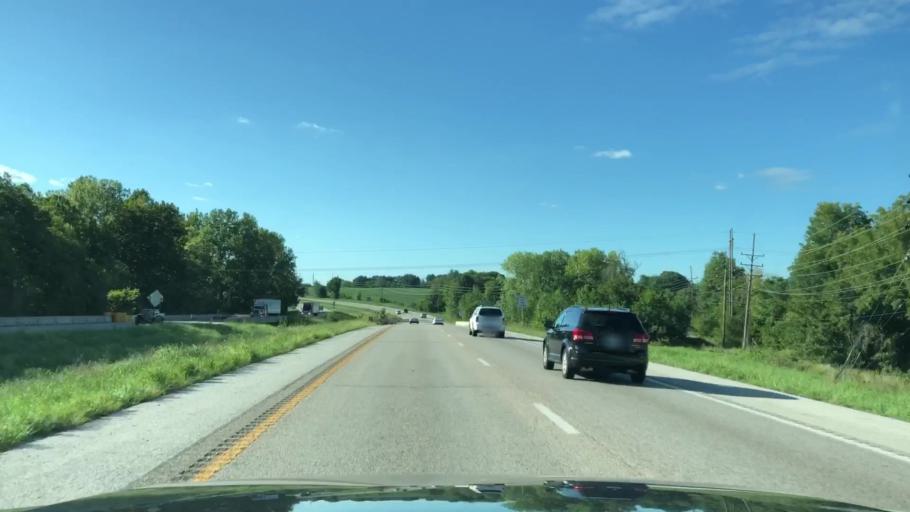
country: US
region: Missouri
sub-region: Saint Charles County
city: Wentzville
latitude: 38.8576
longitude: -90.8735
